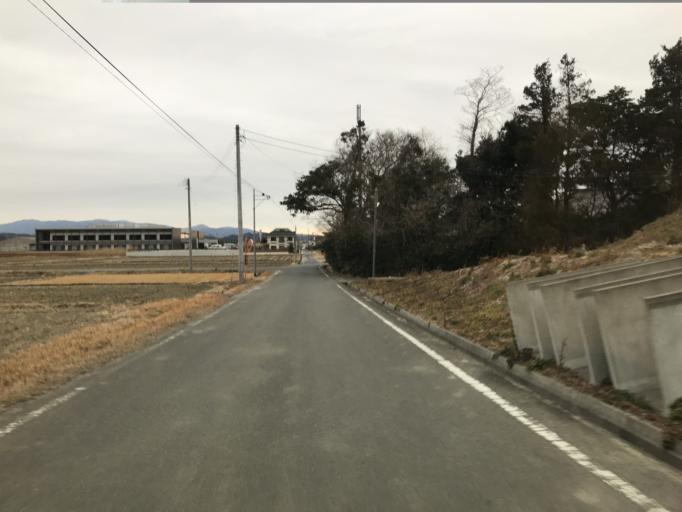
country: JP
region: Fukushima
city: Iwaki
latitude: 37.0509
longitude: 140.9507
